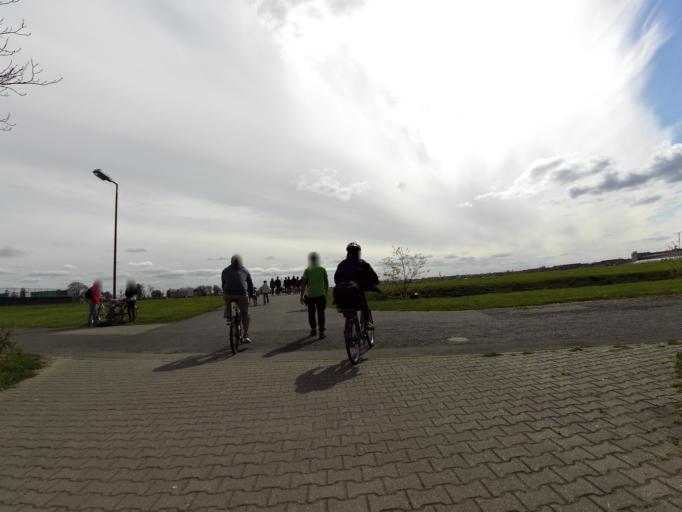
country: DE
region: Berlin
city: Tempelhof Bezirk
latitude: 52.4825
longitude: 13.4025
